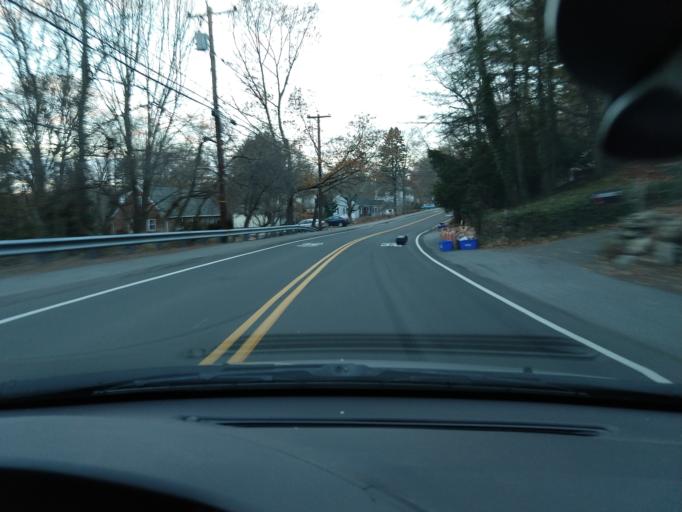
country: US
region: Massachusetts
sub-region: Middlesex County
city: Lexington
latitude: 42.4740
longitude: -71.2387
